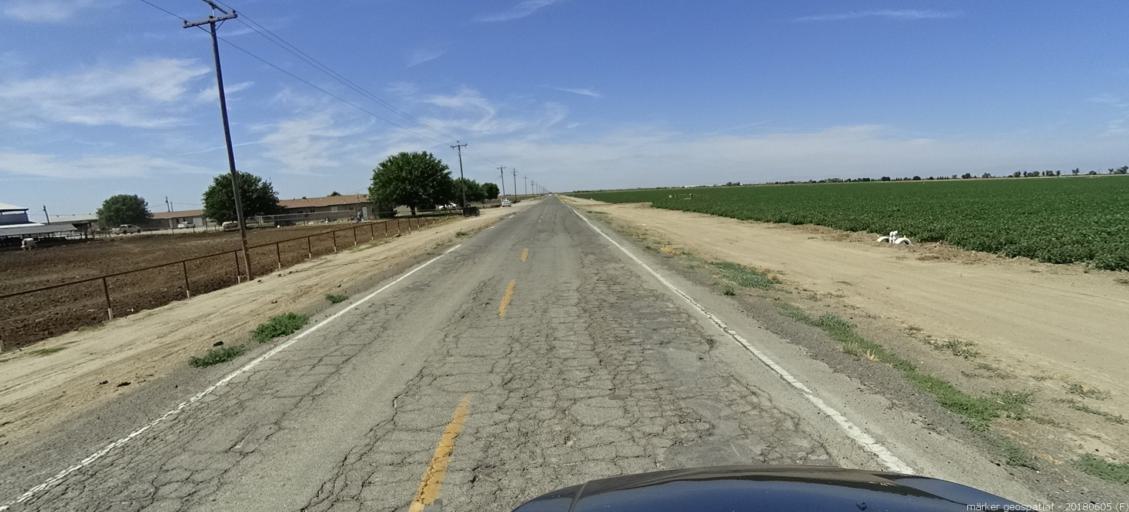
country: US
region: California
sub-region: Fresno County
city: Firebaugh
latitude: 36.9877
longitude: -120.3831
